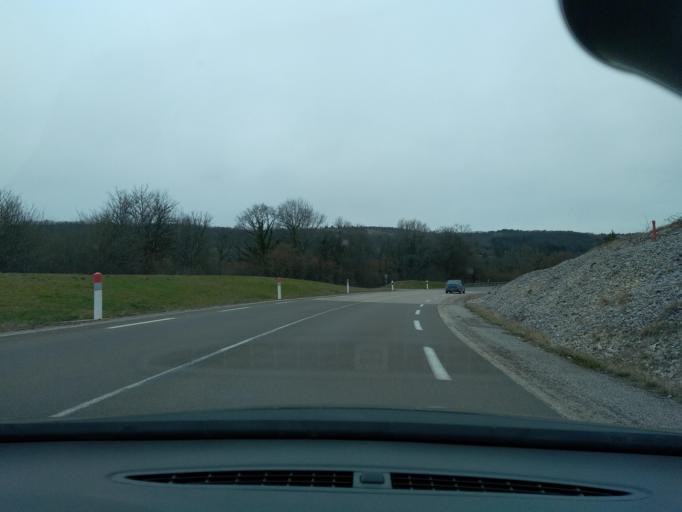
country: FR
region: Franche-Comte
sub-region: Departement du Jura
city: Arinthod
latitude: 46.4138
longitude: 5.5562
